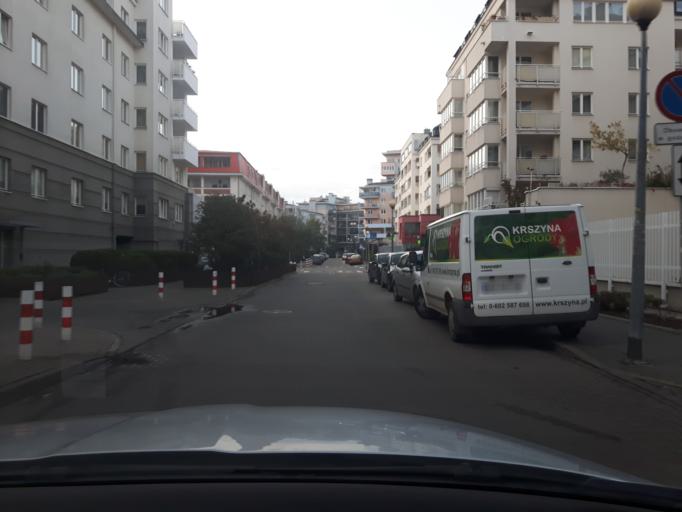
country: PL
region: Masovian Voivodeship
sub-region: Warszawa
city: Kabaty
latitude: 52.1288
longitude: 21.0664
